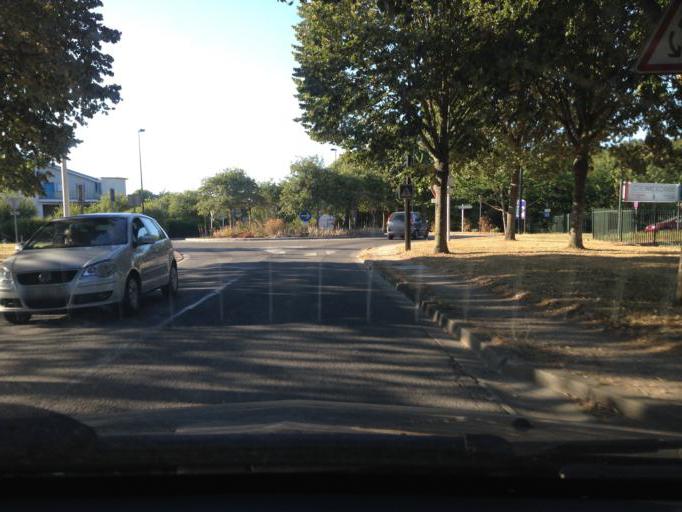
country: FR
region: Ile-de-France
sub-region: Departement des Yvelines
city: Chateaufort
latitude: 48.7282
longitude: 2.0816
